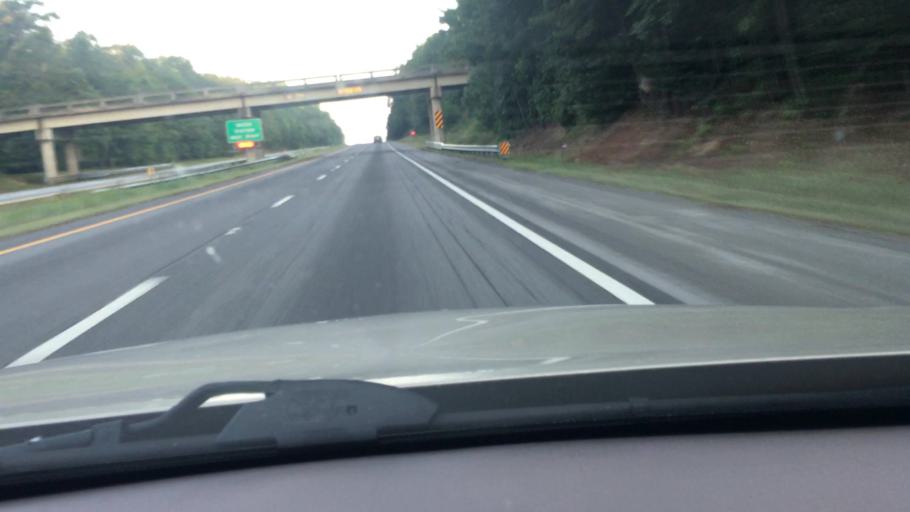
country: US
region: South Carolina
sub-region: Richland County
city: Lake Murray of Richland
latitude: 34.1595
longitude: -81.2724
